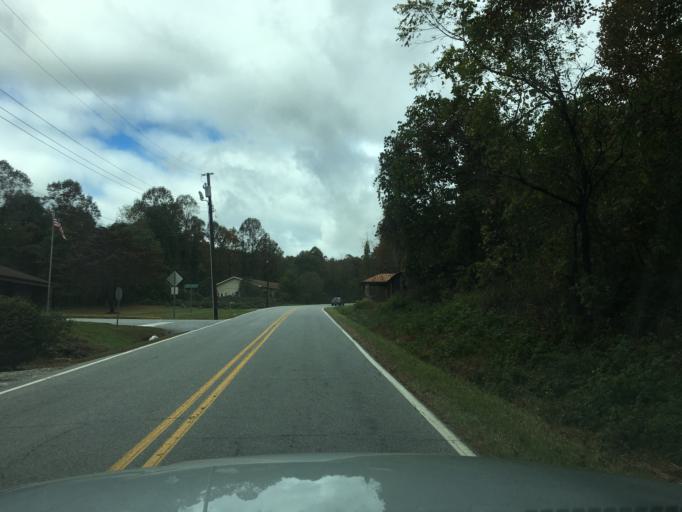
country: US
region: North Carolina
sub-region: Henderson County
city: Flat Rock
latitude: 35.2433
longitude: -82.4177
